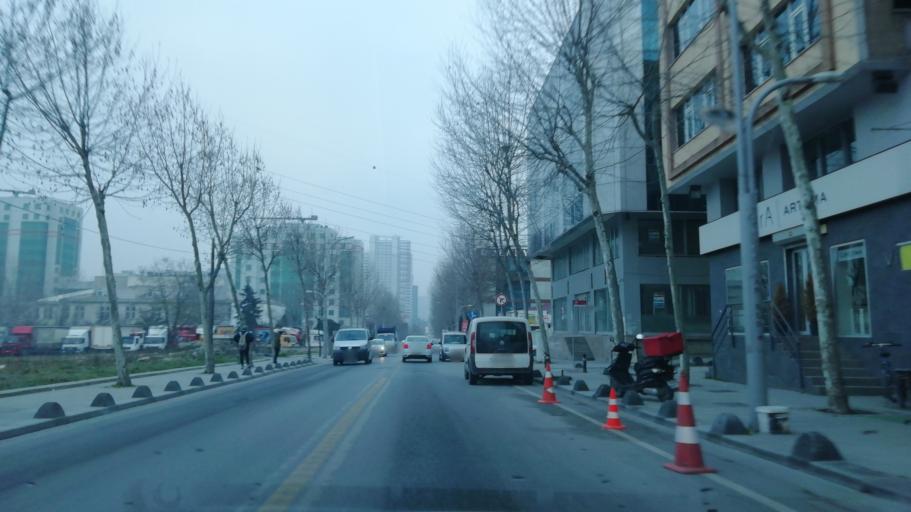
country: TR
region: Istanbul
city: Mahmutbey
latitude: 41.0337
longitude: 28.8144
